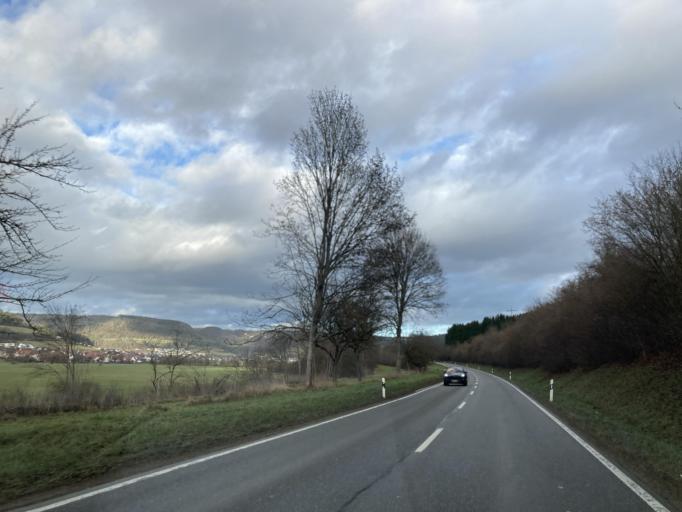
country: DE
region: Baden-Wuerttemberg
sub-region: Freiburg Region
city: Kolbingen
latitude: 48.0097
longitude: 8.8706
